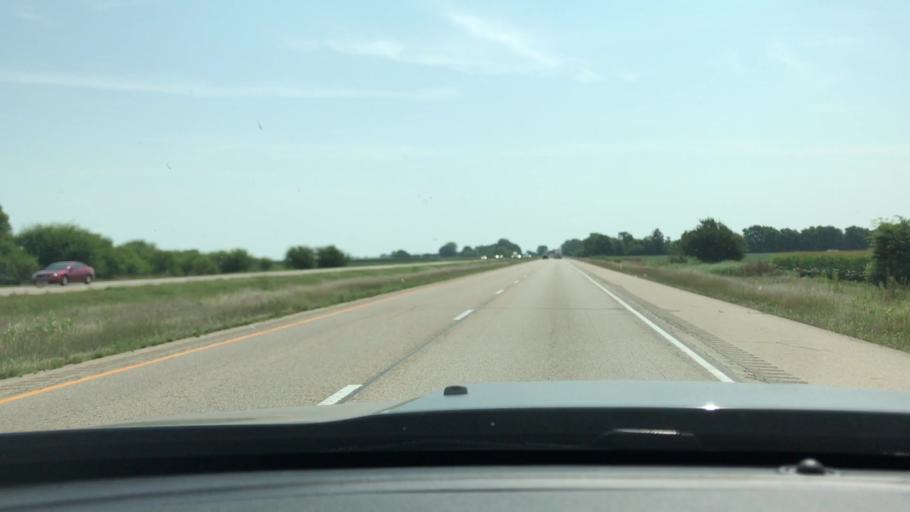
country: US
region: Illinois
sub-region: Henry County
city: Kewanee
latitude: 41.3918
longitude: -89.8495
